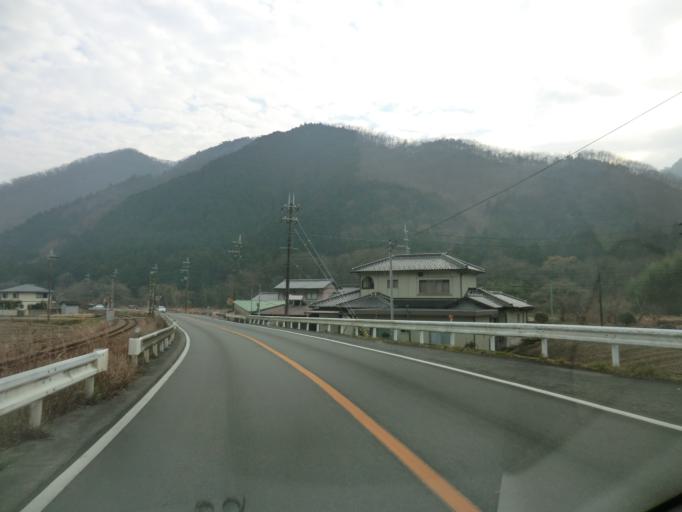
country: JP
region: Hyogo
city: Yamazakicho-nakabirose
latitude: 34.9367
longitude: 134.4771
